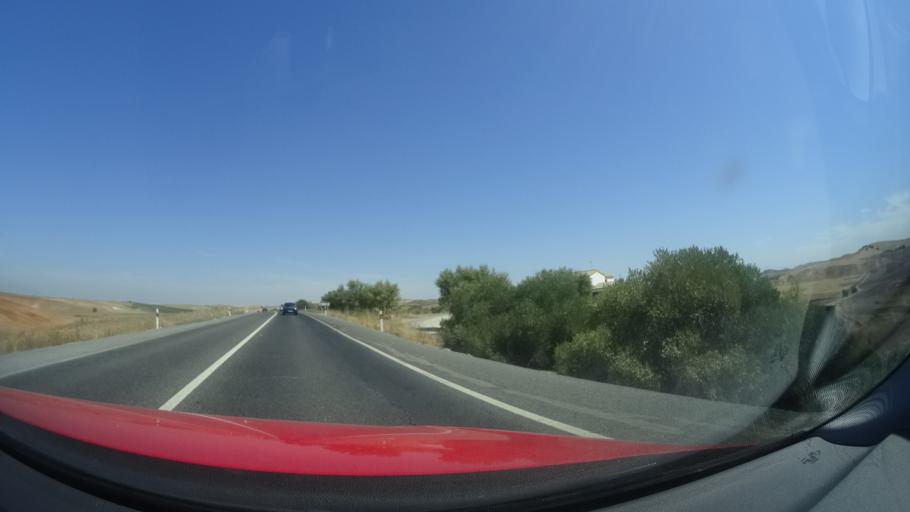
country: ES
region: Andalusia
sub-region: Provincia de Sevilla
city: Las Cabezas de San Juan
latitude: 36.9462
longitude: -5.9052
